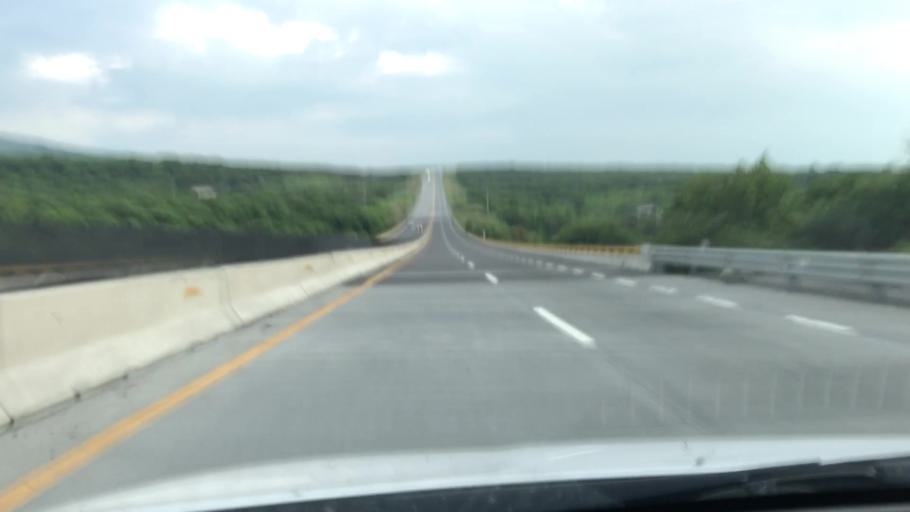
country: MX
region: Jalisco
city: Degollado
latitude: 20.3804
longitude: -102.1209
